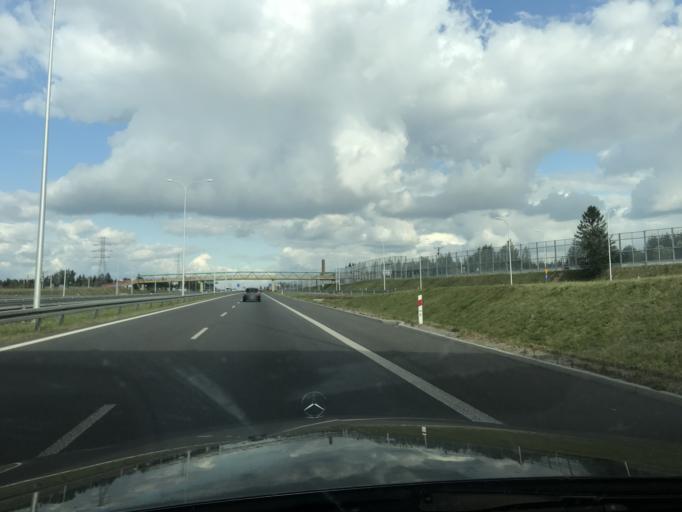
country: PL
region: Lublin Voivodeship
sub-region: Powiat lubelski
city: Jakubowice Murowane
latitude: 51.3032
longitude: 22.5887
